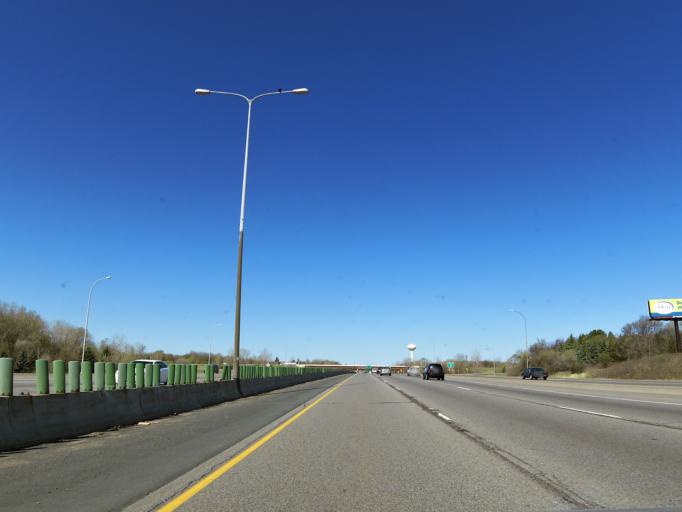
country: US
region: Minnesota
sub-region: Dakota County
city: South Saint Paul
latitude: 44.8748
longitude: -93.0541
